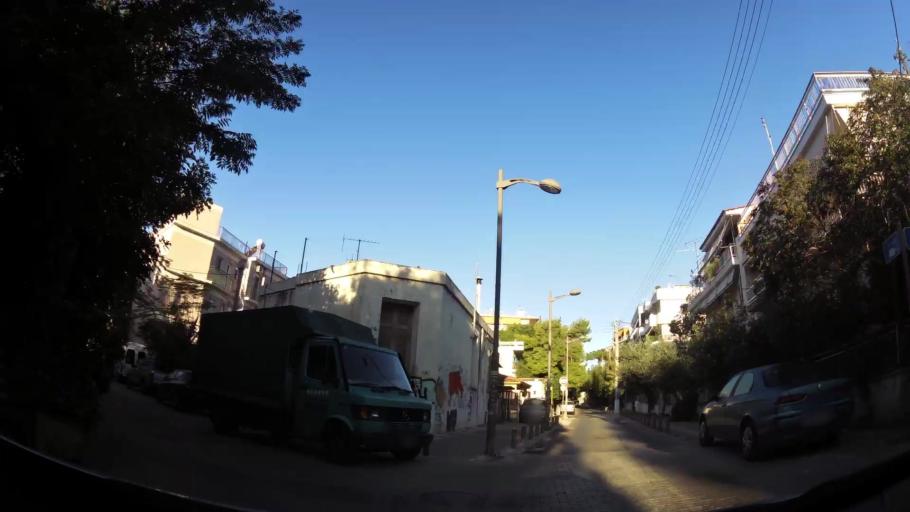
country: GR
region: Attica
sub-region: Nomarchia Athinas
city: Marousi
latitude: 38.0534
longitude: 23.8036
